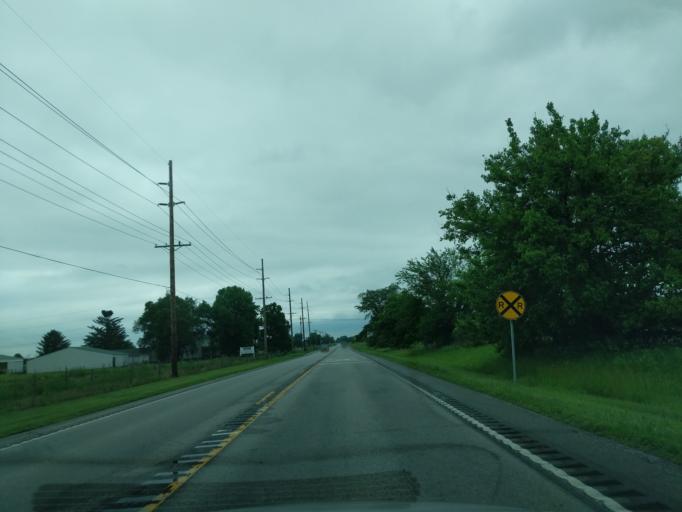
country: US
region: Indiana
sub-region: Hamilton County
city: Cicero
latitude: 40.1040
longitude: -86.0138
